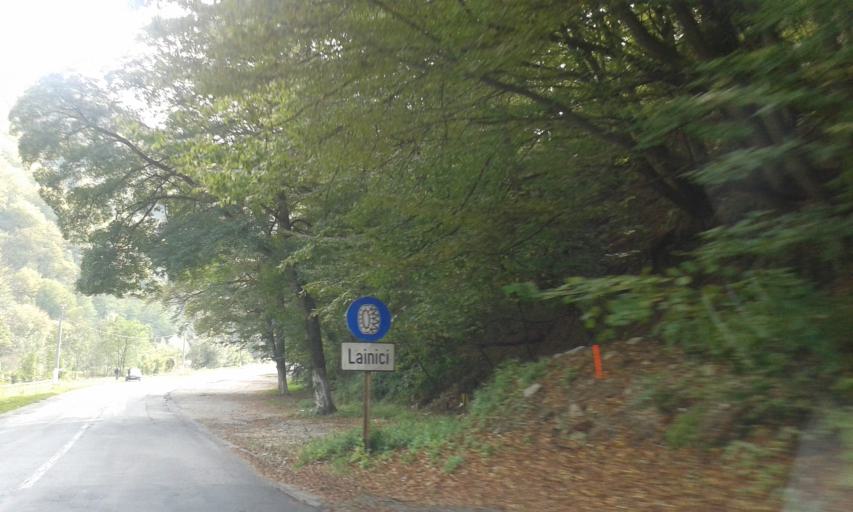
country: RO
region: Gorj
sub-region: Comuna Bumbesti-Jiu
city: Bumbesti-Jiu
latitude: 45.2671
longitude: 23.3909
